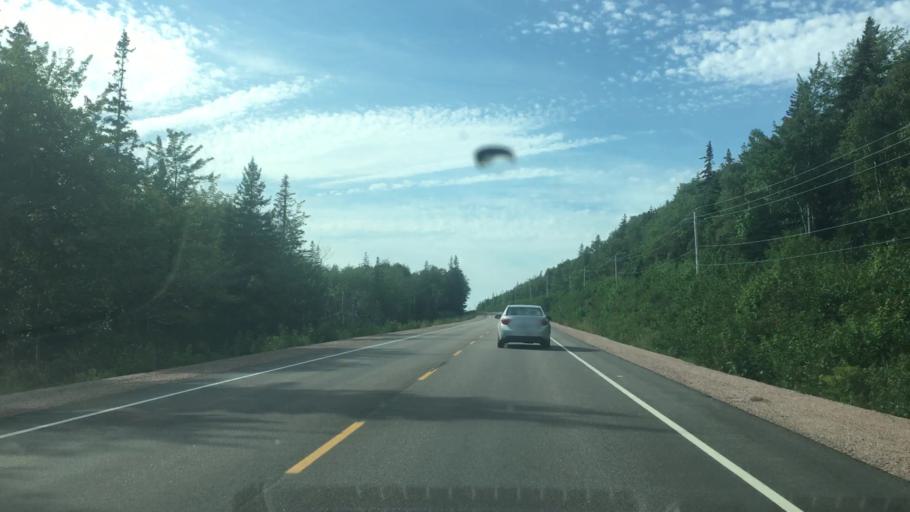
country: CA
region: Nova Scotia
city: Sydney Mines
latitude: 46.8166
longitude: -60.3446
